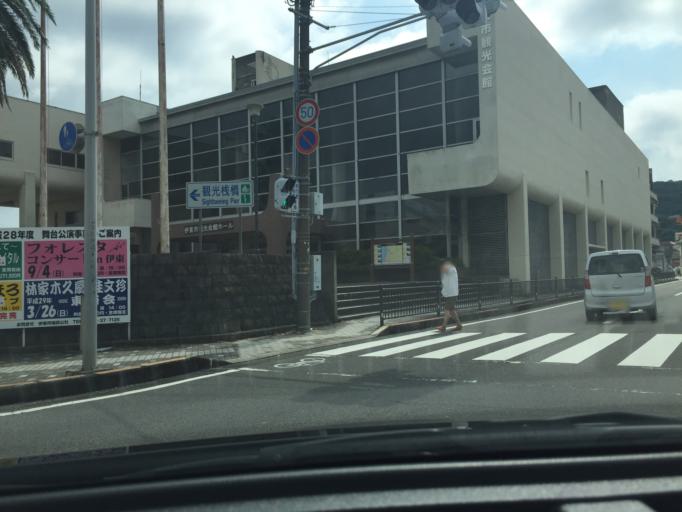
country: JP
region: Shizuoka
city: Ito
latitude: 34.9715
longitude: 139.1016
